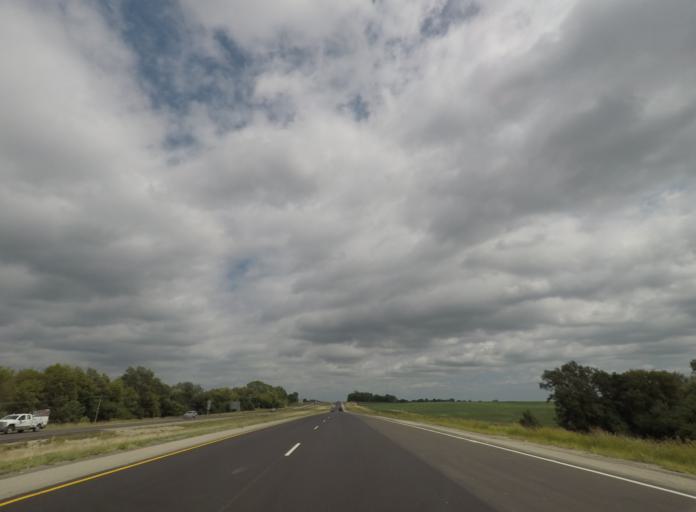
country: US
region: Iowa
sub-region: Linn County
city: Ely
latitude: 41.9265
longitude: -91.6317
